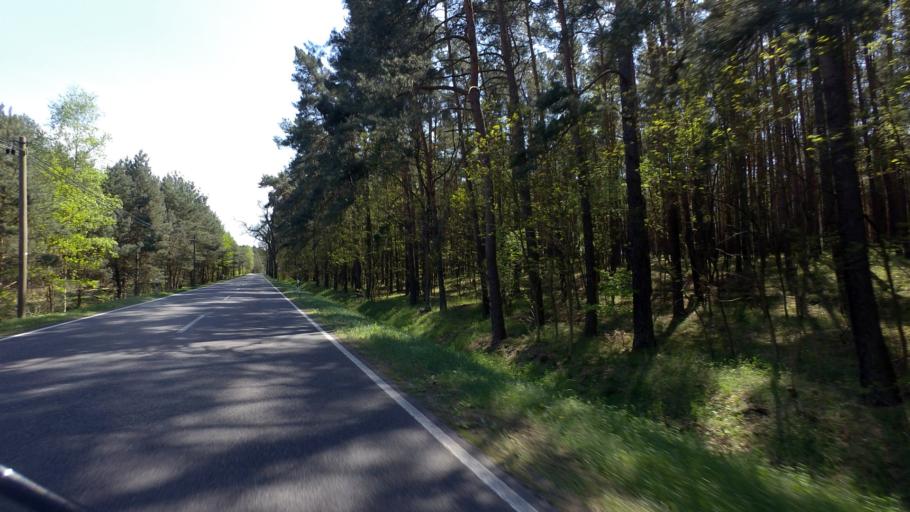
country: DE
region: Brandenburg
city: Lieberose
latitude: 52.0019
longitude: 14.1983
